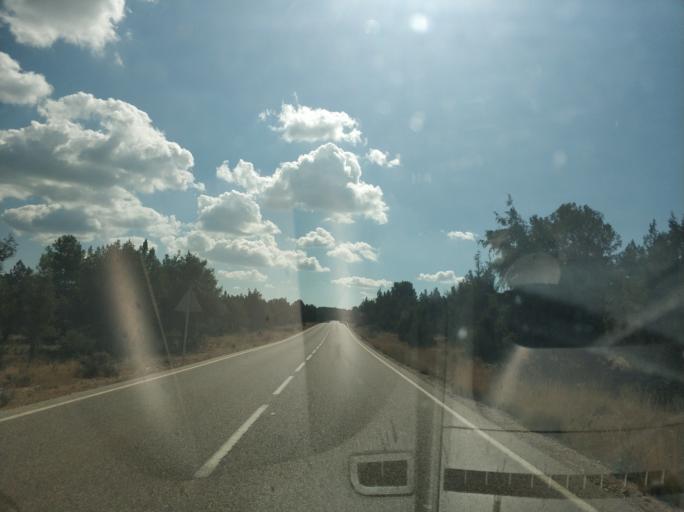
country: ES
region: Castille and Leon
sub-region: Provincia de Soria
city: Ucero
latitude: 41.7374
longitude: -3.0440
